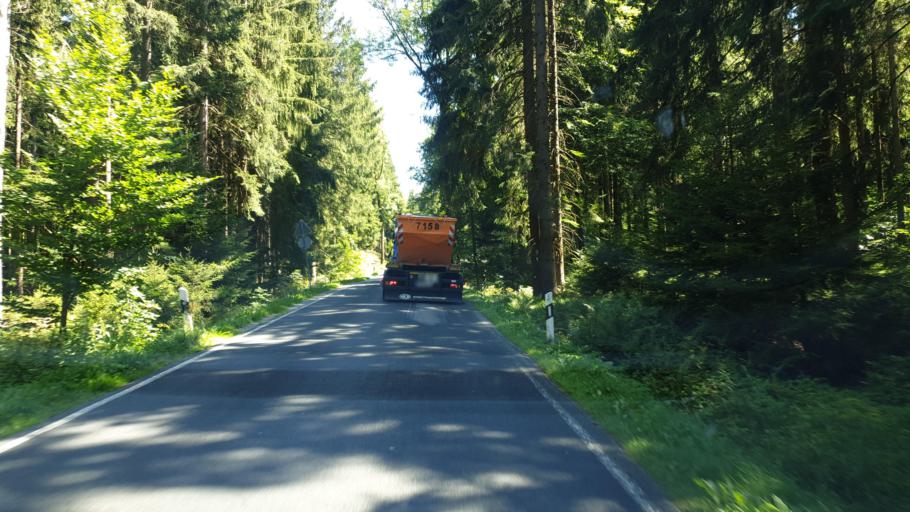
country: DE
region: Saxony
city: Sosa
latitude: 50.5063
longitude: 12.6770
